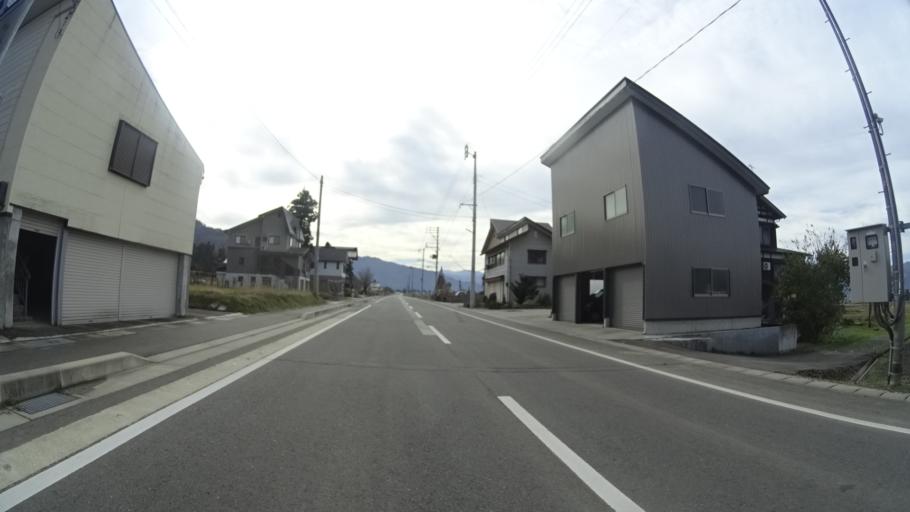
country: JP
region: Niigata
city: Muikamachi
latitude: 37.0386
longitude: 138.8914
